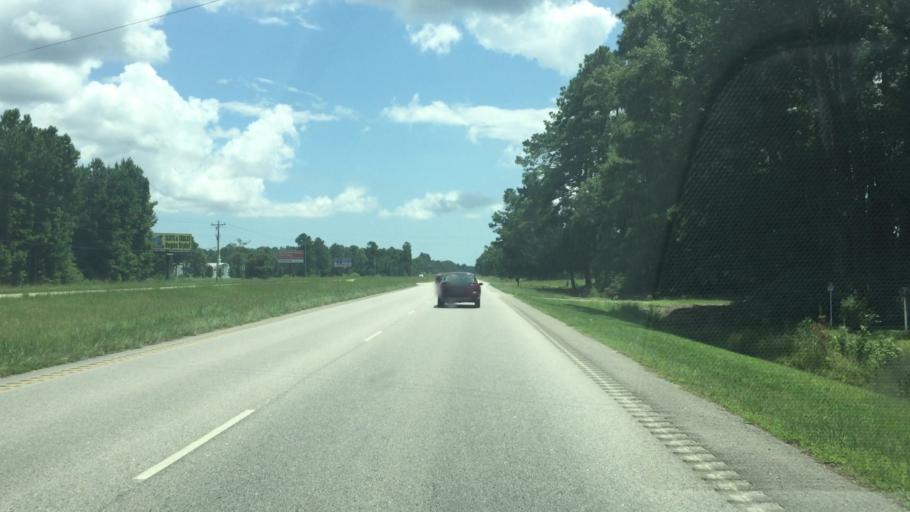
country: US
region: South Carolina
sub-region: Horry County
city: Little River
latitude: 33.9732
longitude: -78.7420
